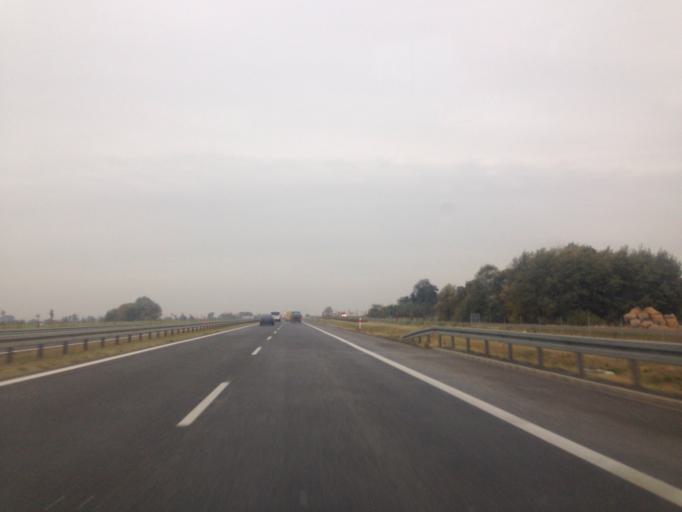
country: PL
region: Greater Poland Voivodeship
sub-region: Powiat poznanski
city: Kleszczewo
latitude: 52.3484
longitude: 17.1769
